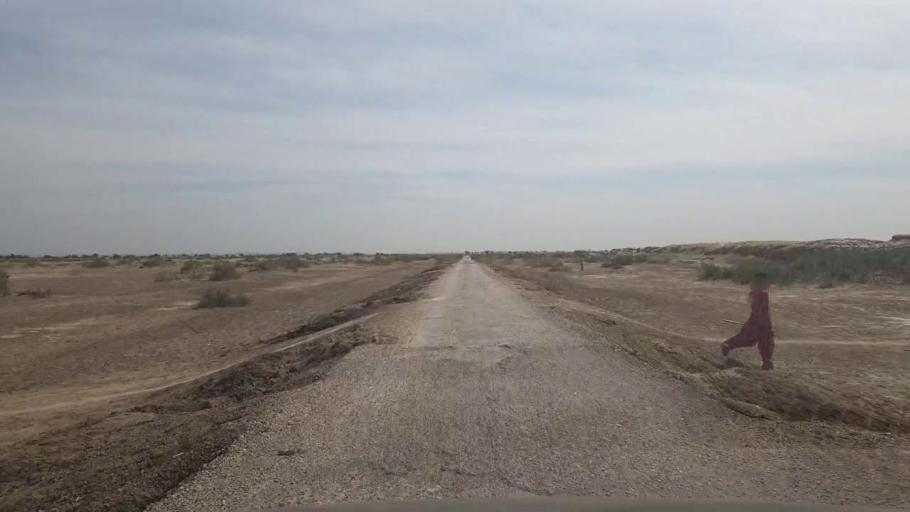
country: PK
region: Sindh
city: Kunri
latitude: 25.2191
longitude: 69.6205
